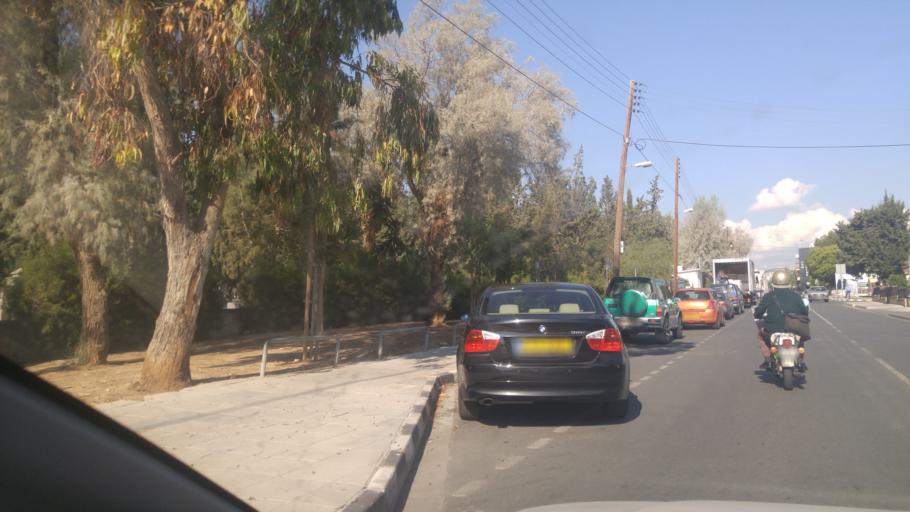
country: CY
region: Limassol
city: Limassol
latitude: 34.6912
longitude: 33.0573
